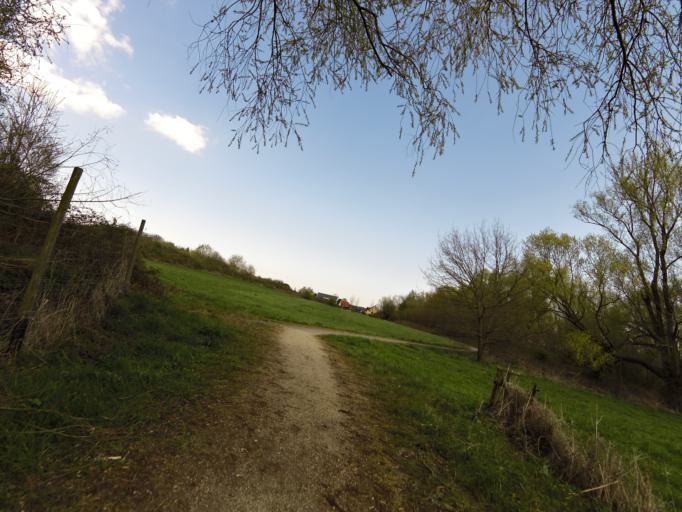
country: DE
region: North Rhine-Westphalia
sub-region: Regierungsbezirk Koln
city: Alfter
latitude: 50.6861
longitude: 7.0170
